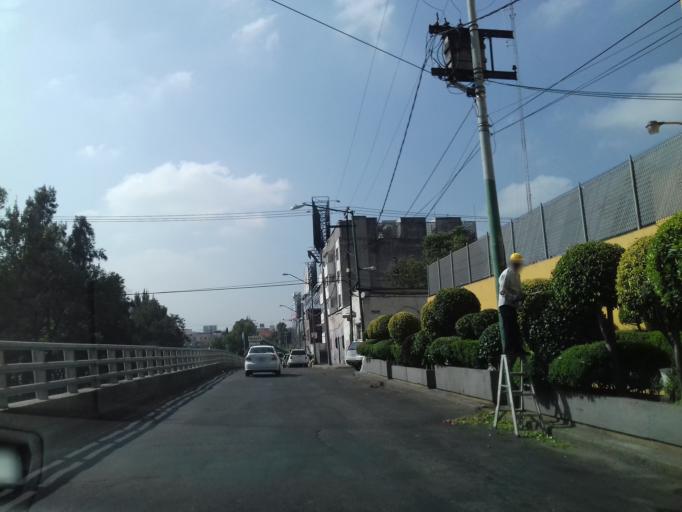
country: MX
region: Mexico City
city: Polanco
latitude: 19.4011
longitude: -99.1865
